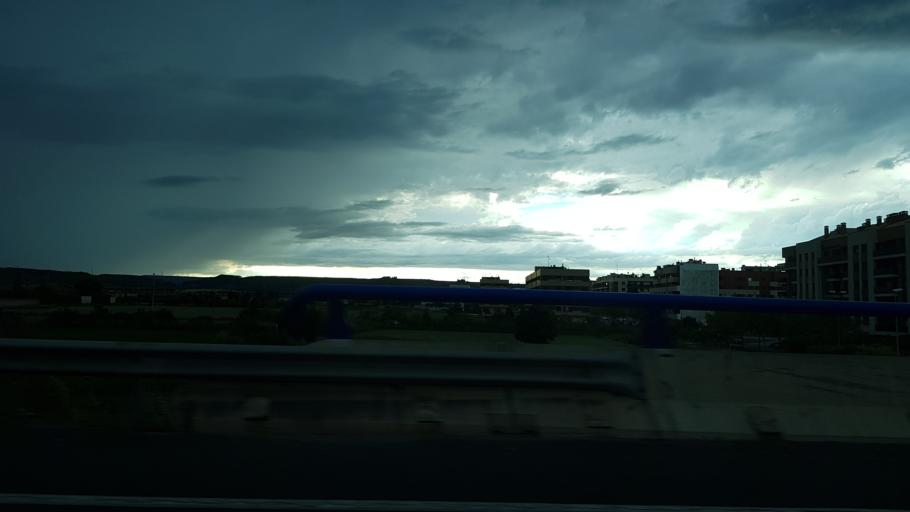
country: ES
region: La Rioja
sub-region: Provincia de La Rioja
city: Logrono
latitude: 42.4496
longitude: -2.4584
